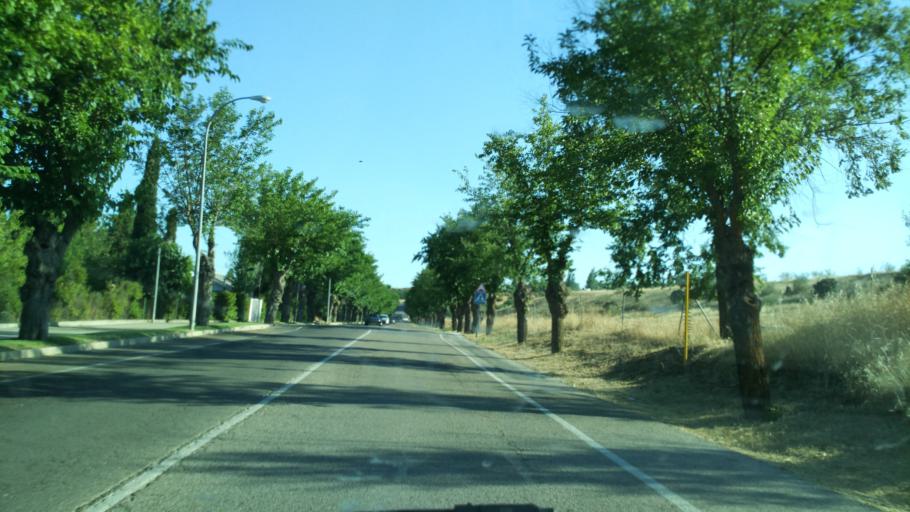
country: ES
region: Madrid
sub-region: Provincia de Madrid
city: San Agustin de Guadalix
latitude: 40.6896
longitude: -3.6102
